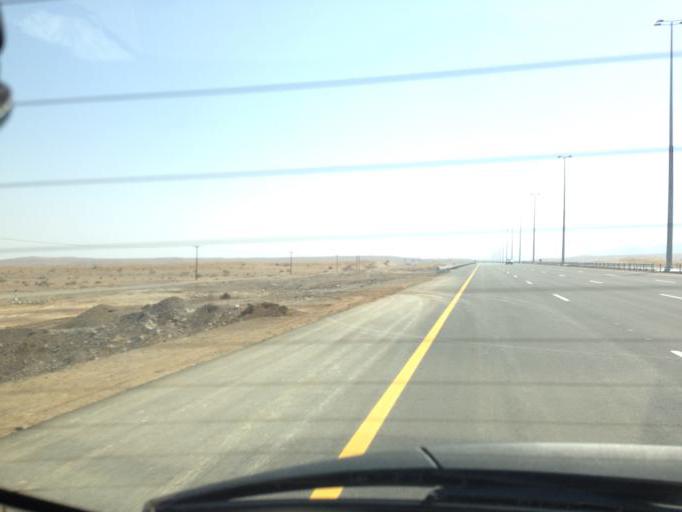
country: OM
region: Al Batinah
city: Rustaq
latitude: 23.5255
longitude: 57.6047
